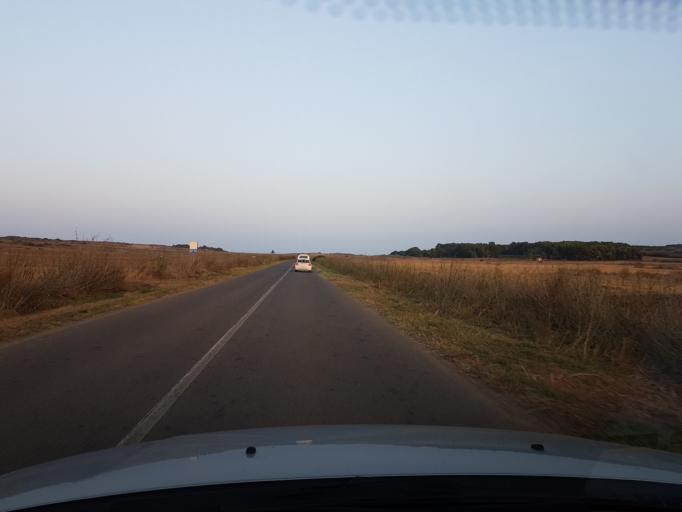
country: IT
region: Sardinia
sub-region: Provincia di Oristano
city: Cabras
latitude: 39.9411
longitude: 8.4385
